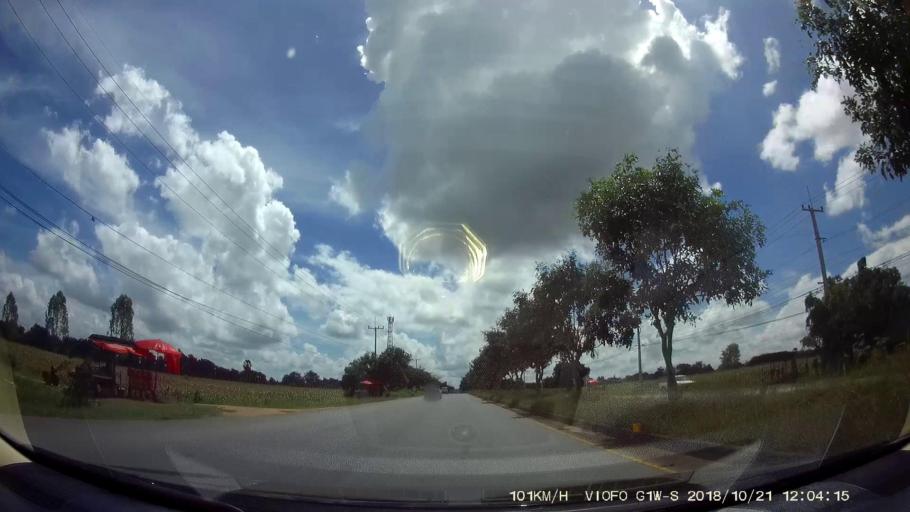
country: TH
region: Chaiyaphum
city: Chatturat
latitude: 15.4973
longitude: 101.8208
